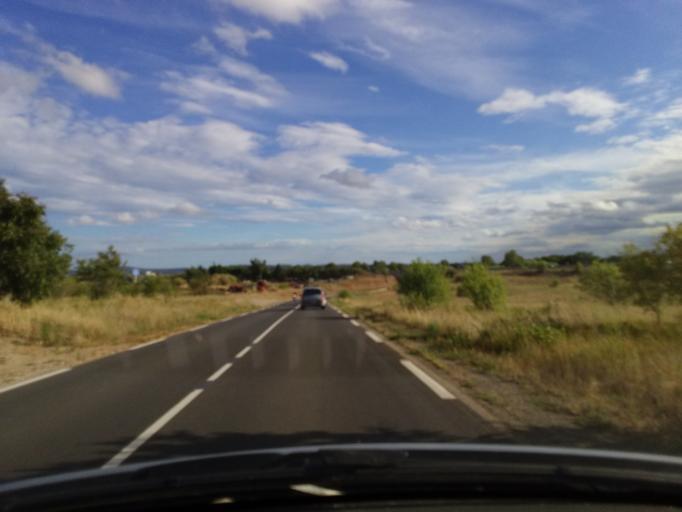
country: FR
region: Languedoc-Roussillon
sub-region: Departement de l'Herault
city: Saint-Andre-de-Sangonis
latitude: 43.6597
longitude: 3.5179
